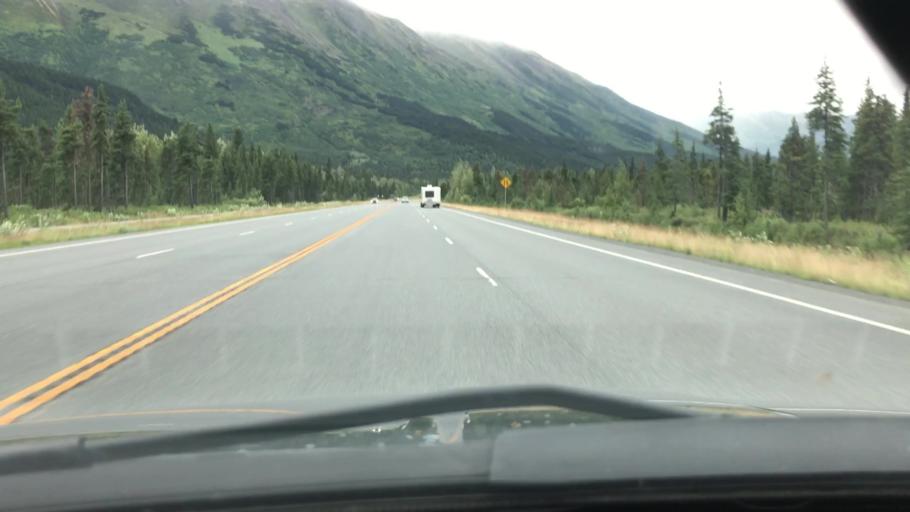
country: US
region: Alaska
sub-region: Anchorage Municipality
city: Girdwood
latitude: 60.7293
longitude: -149.3208
